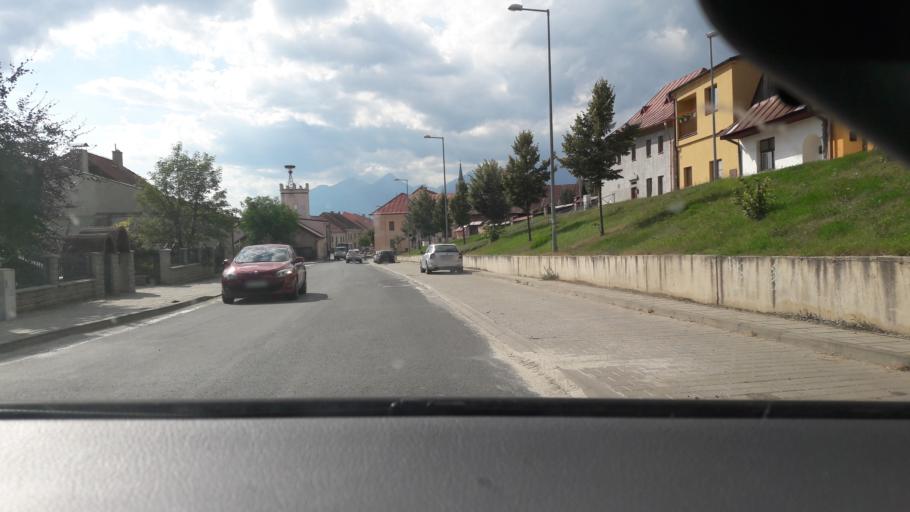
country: SK
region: Presovsky
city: Lubica
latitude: 49.1206
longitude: 20.4510
